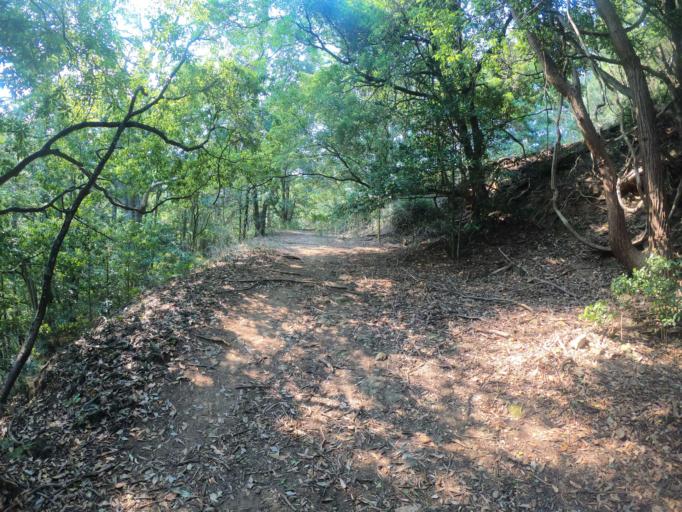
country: AU
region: New South Wales
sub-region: Wollongong
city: Bulli
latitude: -34.3245
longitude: 150.8884
